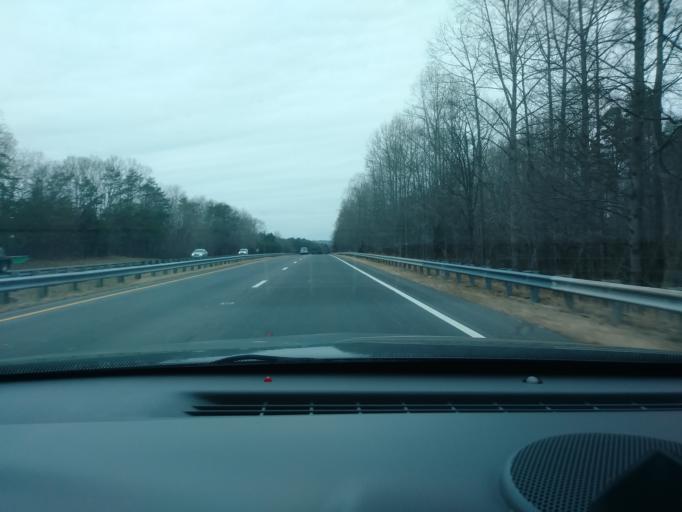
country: US
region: North Carolina
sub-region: Forsyth County
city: Lewisville
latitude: 36.1017
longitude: -80.4904
